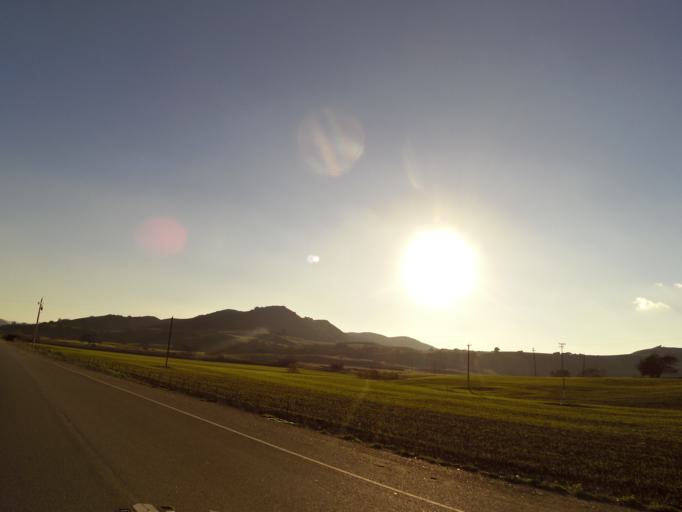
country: US
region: California
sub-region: Santa Clara County
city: Gilroy
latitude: 36.9477
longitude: -121.5532
